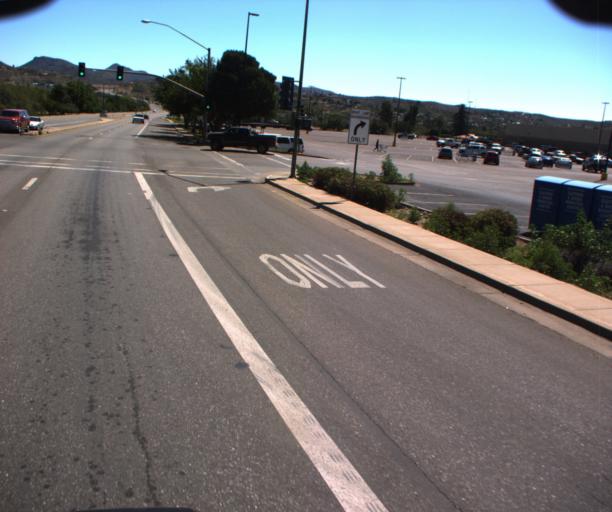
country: US
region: Arizona
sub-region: Gila County
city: Claypool
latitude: 33.4137
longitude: -110.8375
